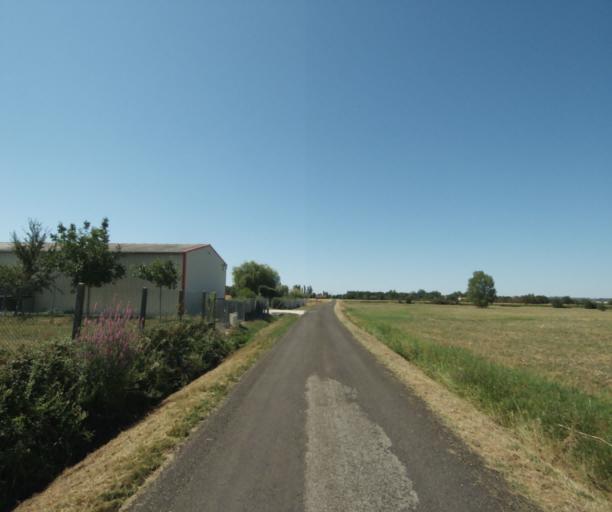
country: FR
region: Midi-Pyrenees
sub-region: Departement de la Haute-Garonne
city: Revel
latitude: 43.4735
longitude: 1.9844
